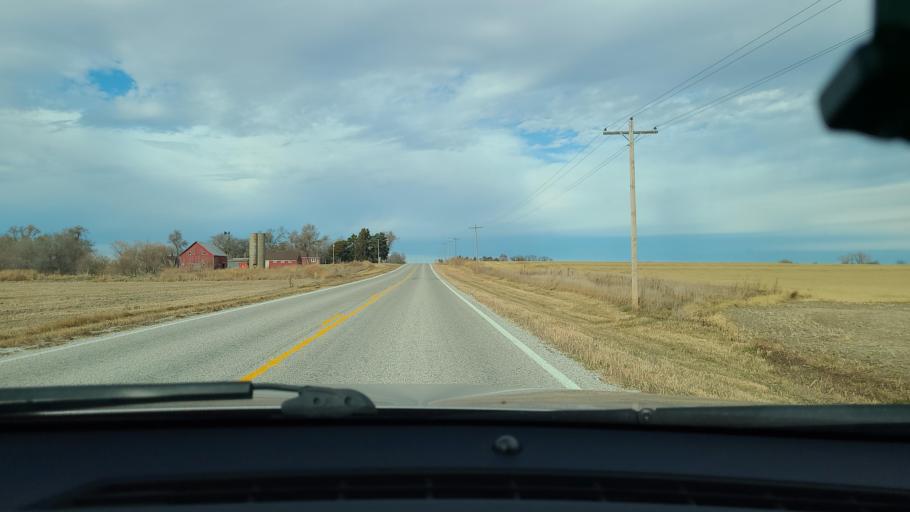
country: US
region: Kansas
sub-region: McPherson County
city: Inman
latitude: 38.2927
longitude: -97.9250
